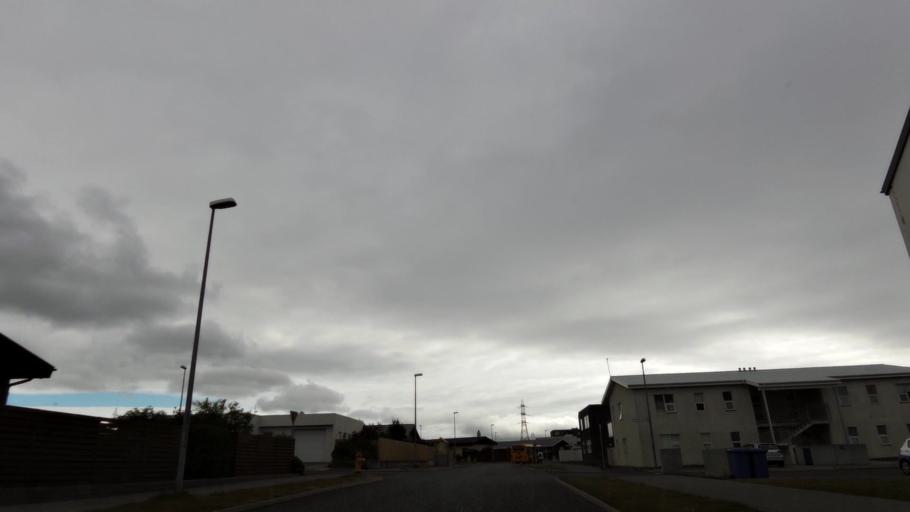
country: IS
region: Capital Region
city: Hafnarfjoerdur
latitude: 64.0440
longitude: -21.9783
